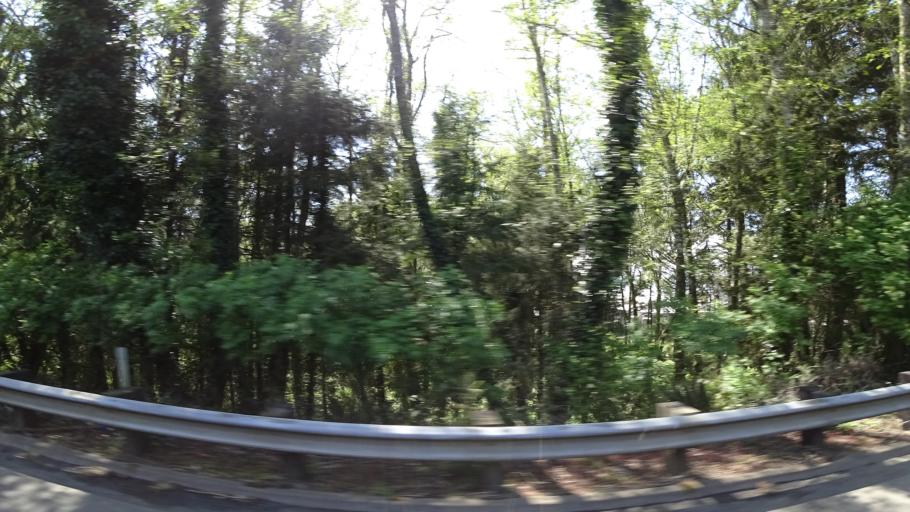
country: US
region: Oregon
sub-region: Lincoln County
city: Newport
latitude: 44.6633
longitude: -124.0554
